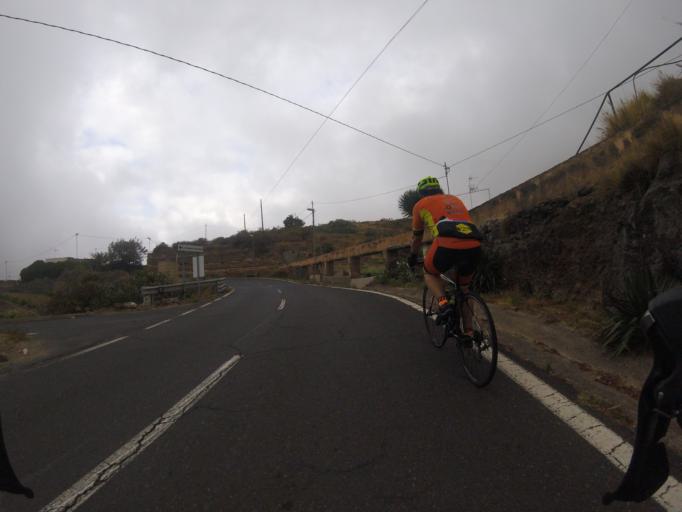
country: ES
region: Canary Islands
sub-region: Provincia de Santa Cruz de Tenerife
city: Guimar
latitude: 28.2779
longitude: -16.4113
